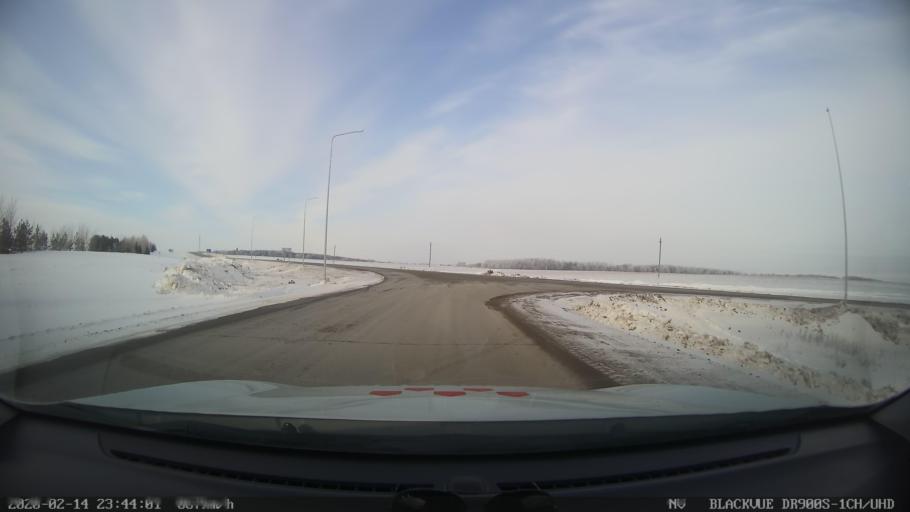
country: RU
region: Tatarstan
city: Kuybyshevskiy Zaton
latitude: 55.2088
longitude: 49.2471
